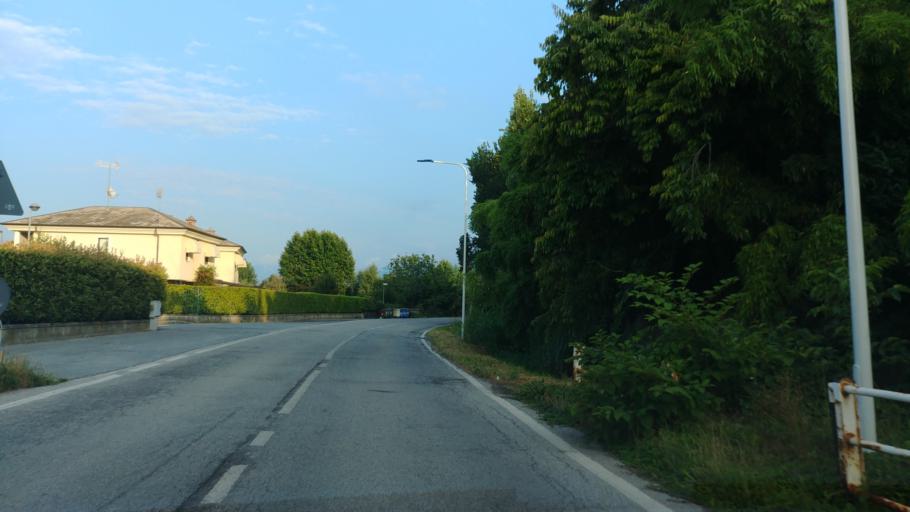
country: IT
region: Piedmont
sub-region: Provincia di Cuneo
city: Cuneo
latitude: 44.3780
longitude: 7.5730
